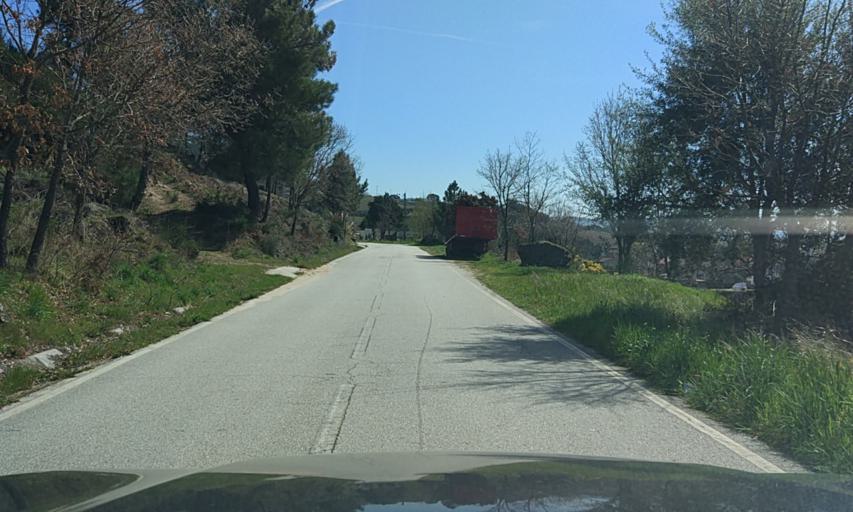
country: PT
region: Vila Real
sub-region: Sabrosa
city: Sabrosa
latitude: 41.3361
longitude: -7.5791
